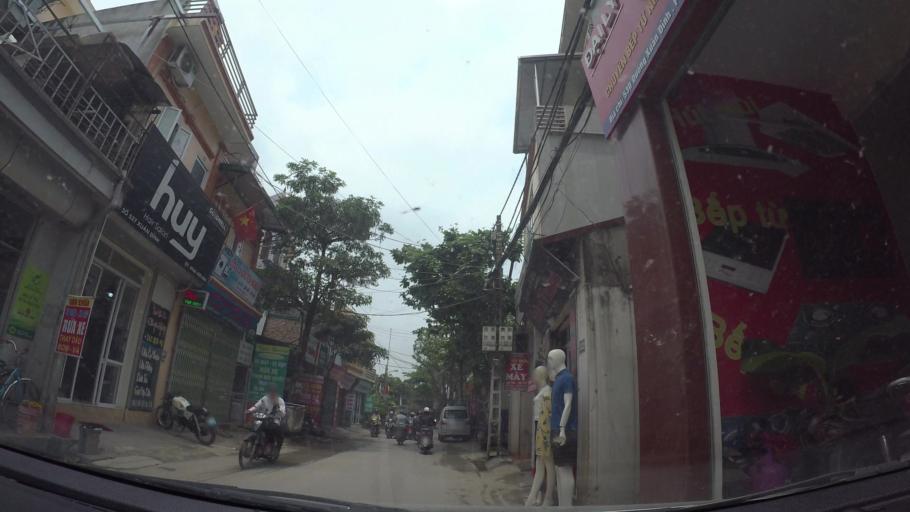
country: VN
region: Ha Noi
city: Tay Ho
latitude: 21.0753
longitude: 105.7884
